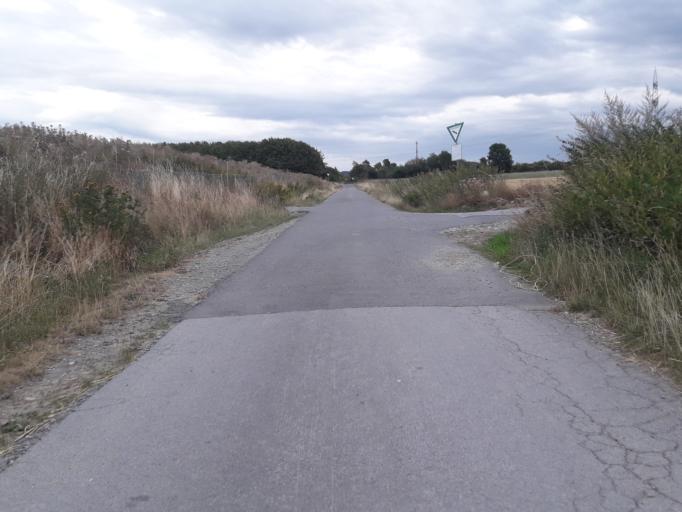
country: DE
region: North Rhine-Westphalia
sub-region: Regierungsbezirk Detmold
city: Paderborn
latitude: 51.6953
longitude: 8.7181
